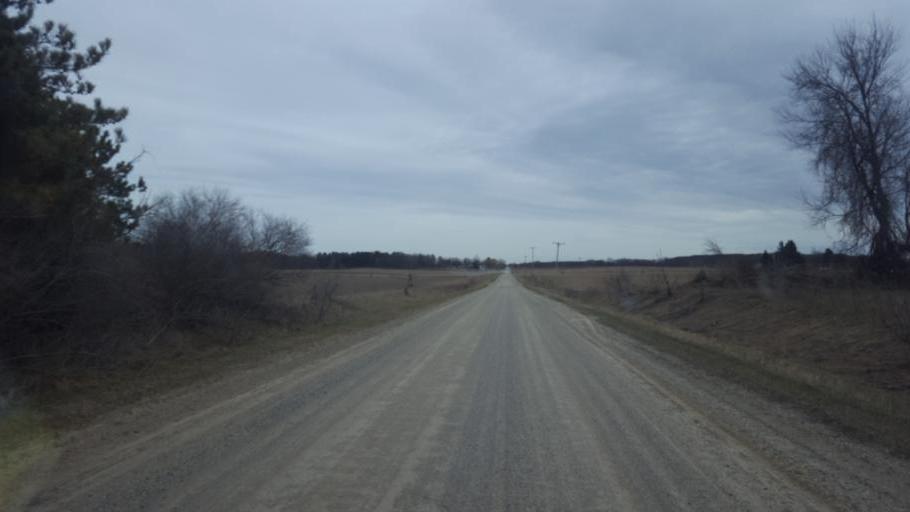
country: US
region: Michigan
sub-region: Montcalm County
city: Edmore
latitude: 43.4513
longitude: -85.0299
